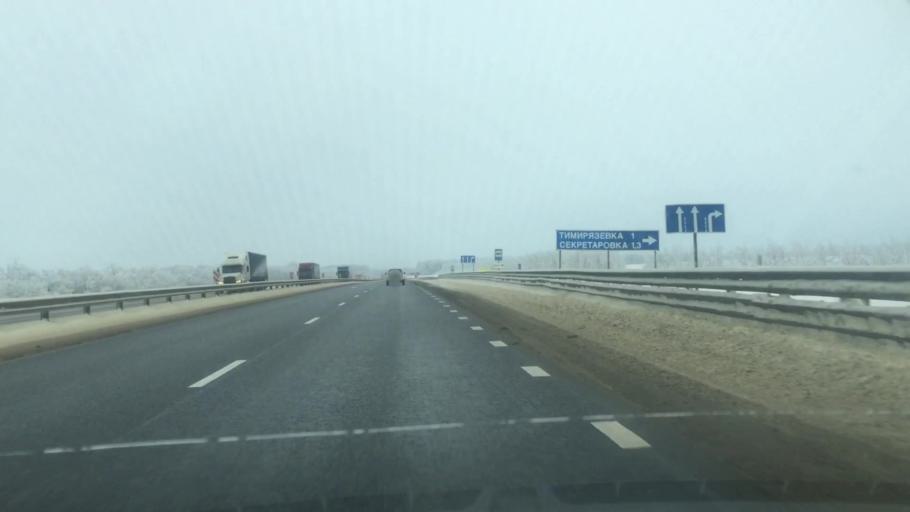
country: RU
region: Lipetsk
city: Zadonsk
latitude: 52.5035
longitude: 38.7555
